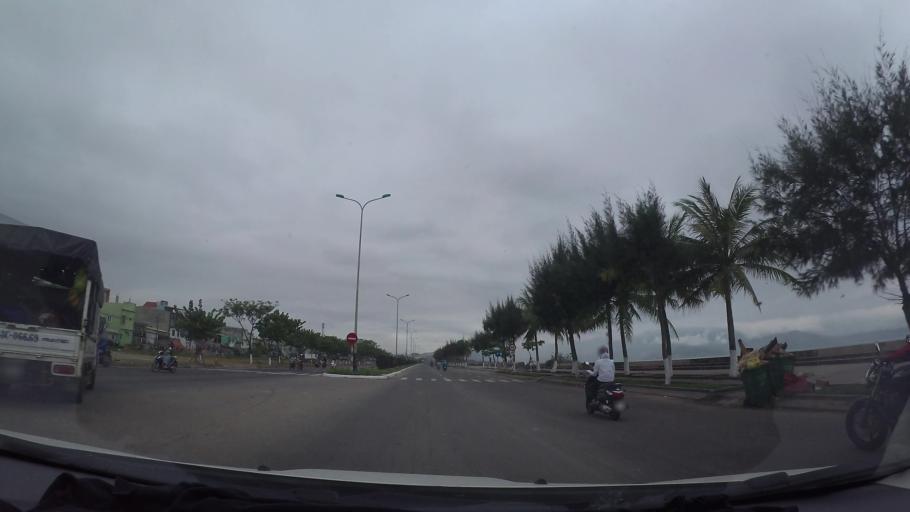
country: VN
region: Da Nang
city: Lien Chieu
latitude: 16.0828
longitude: 108.1635
